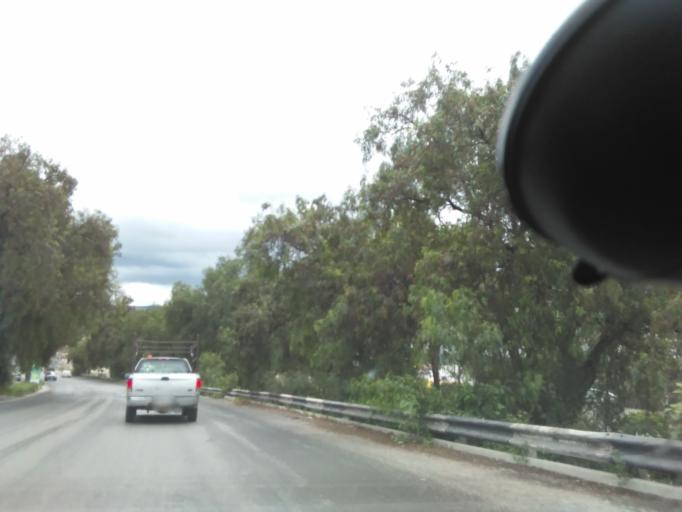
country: MX
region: Hidalgo
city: San Marcos
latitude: 20.0557
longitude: -99.3319
